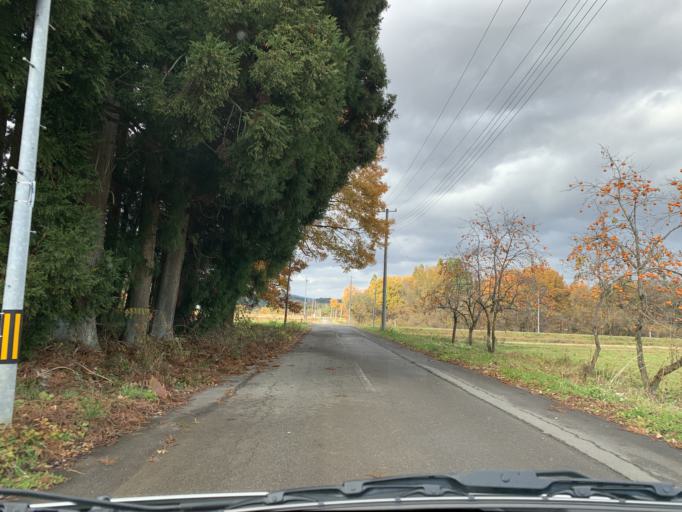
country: JP
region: Iwate
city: Mizusawa
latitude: 39.1145
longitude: 140.9735
